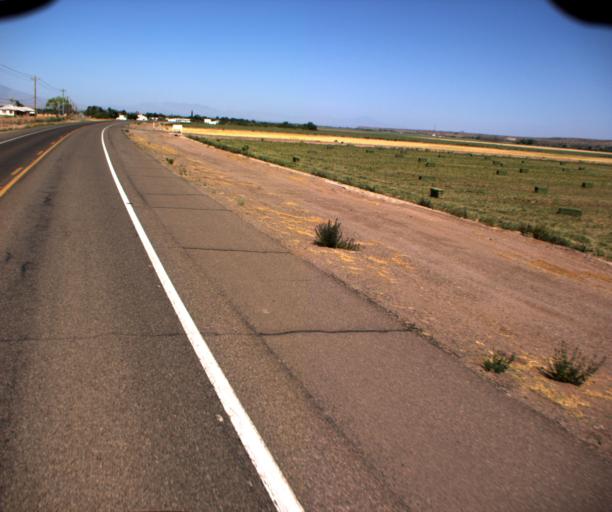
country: US
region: Arizona
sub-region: Graham County
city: Safford
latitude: 32.8129
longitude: -109.6149
